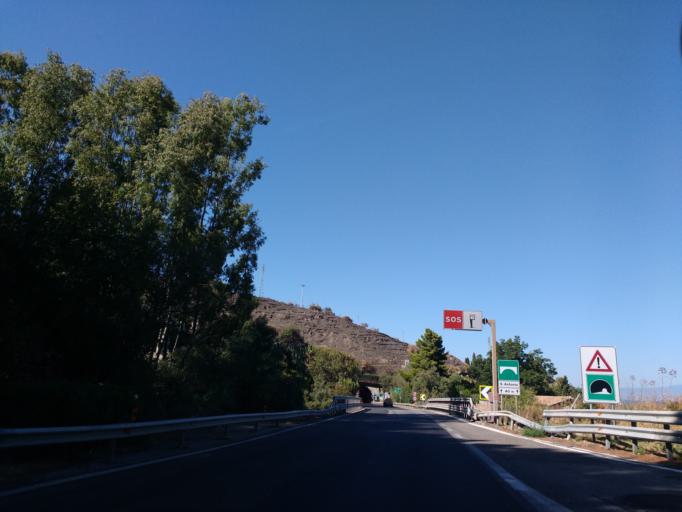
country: IT
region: Sicily
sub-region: Messina
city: Taormina
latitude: 37.8600
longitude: 15.2935
